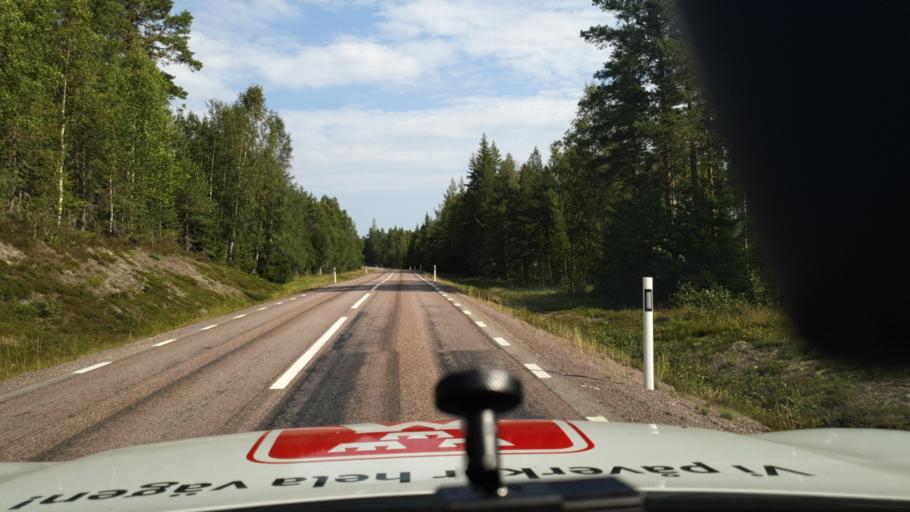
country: SE
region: Vaermland
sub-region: Hagfors Kommun
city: Ekshaerad
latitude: 60.4878
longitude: 13.4105
